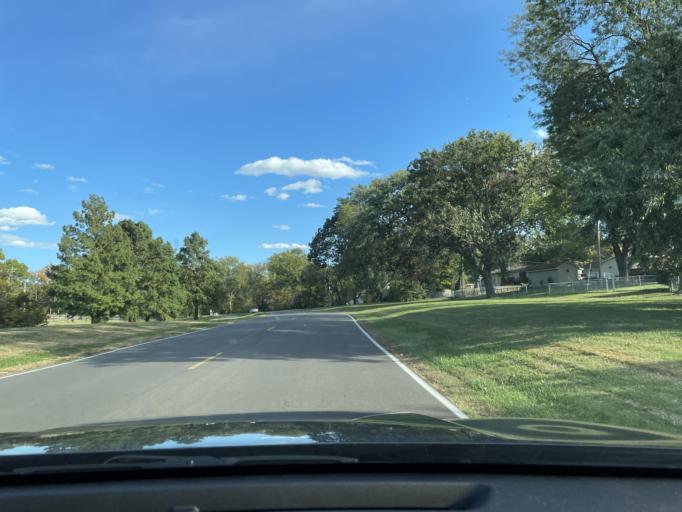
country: US
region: Missouri
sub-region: Buchanan County
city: Saint Joseph
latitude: 39.7281
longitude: -94.8418
